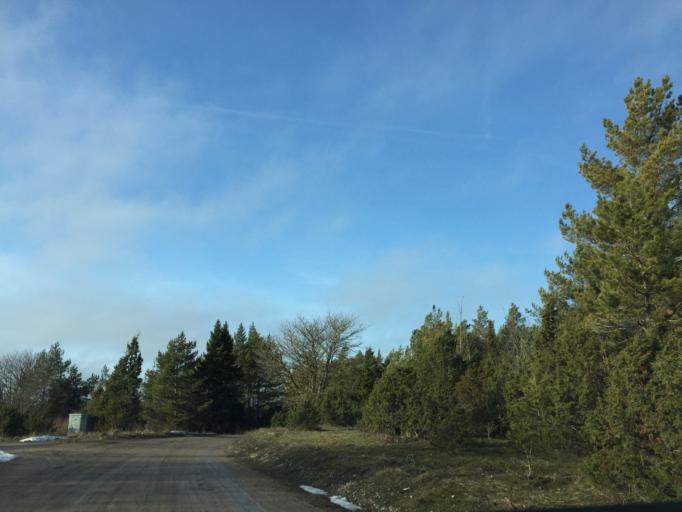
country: EE
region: Saare
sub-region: Kuressaare linn
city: Kuressaare
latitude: 58.4710
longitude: 21.9630
